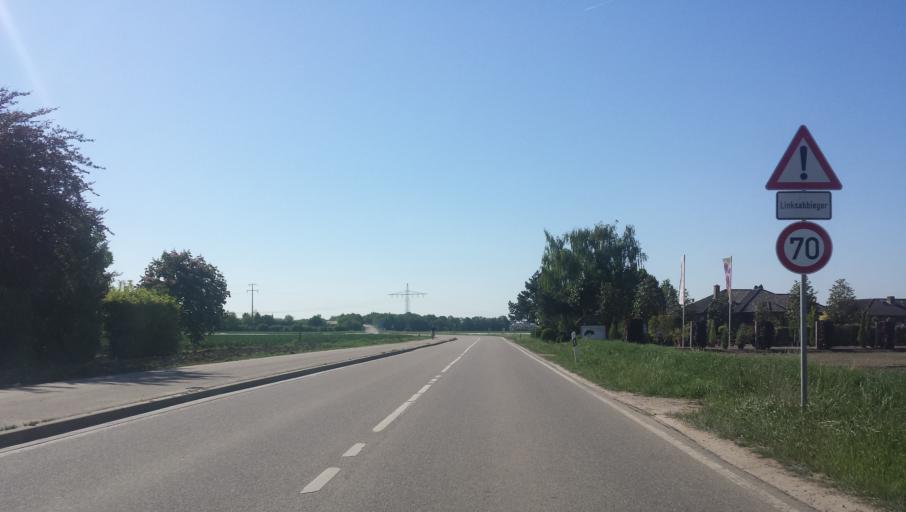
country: DE
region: Rheinland-Pfalz
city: Mutterstadt
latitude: 49.4578
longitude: 8.3379
